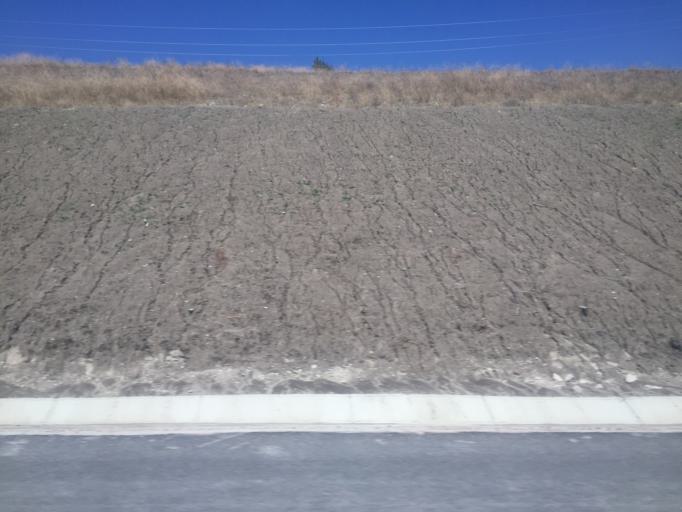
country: TR
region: Balikesir
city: Gobel
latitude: 39.9736
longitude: 28.1661
